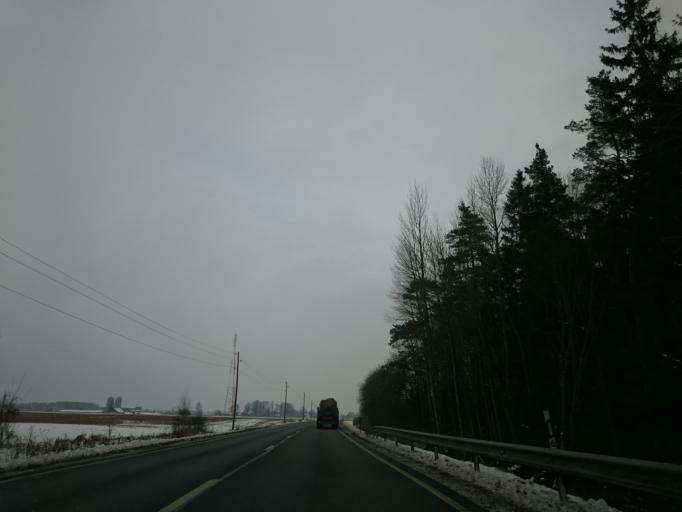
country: LV
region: Krimulda
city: Ragana
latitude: 57.2167
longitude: 24.7866
